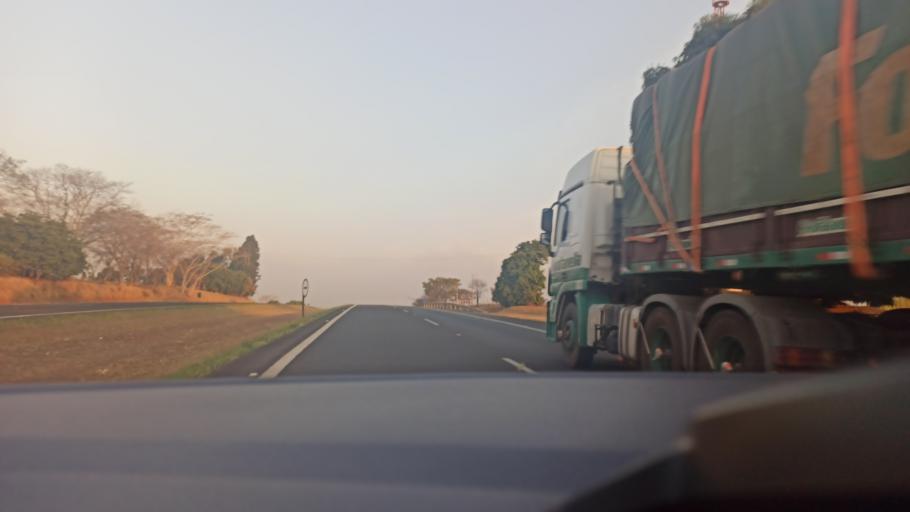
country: BR
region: Sao Paulo
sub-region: Taquaritinga
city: Taquaritinga
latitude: -21.4131
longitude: -48.6890
